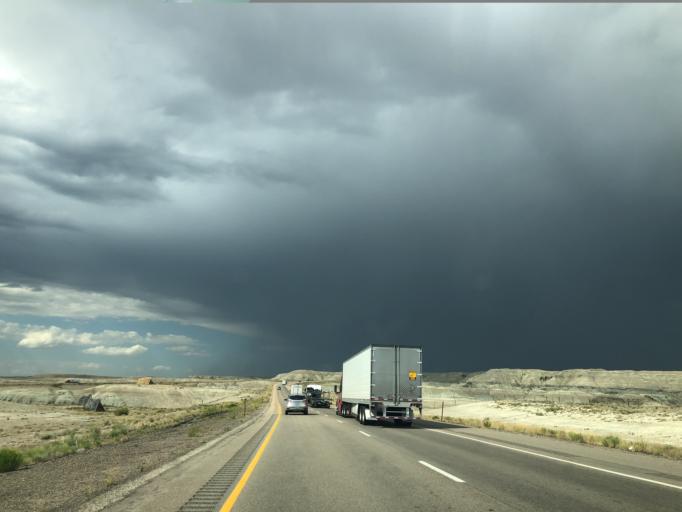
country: US
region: Wyoming
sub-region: Uinta County
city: Lyman
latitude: 41.4172
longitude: -110.1314
